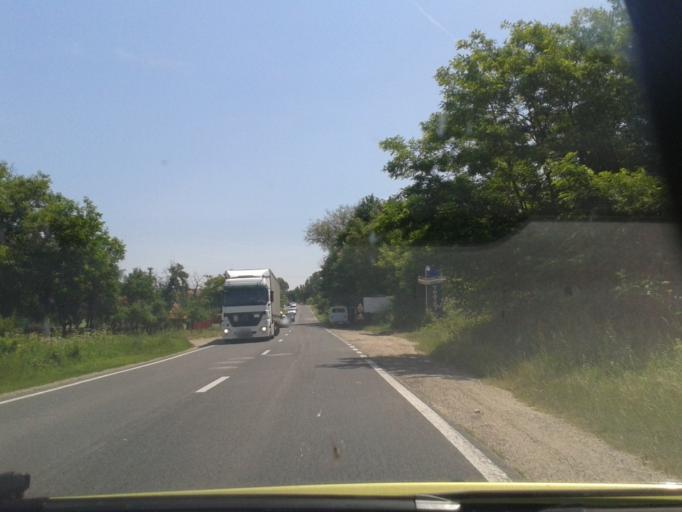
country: RO
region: Timis
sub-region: Comuna Curtea
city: Curtea
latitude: 45.8484
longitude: 22.3063
